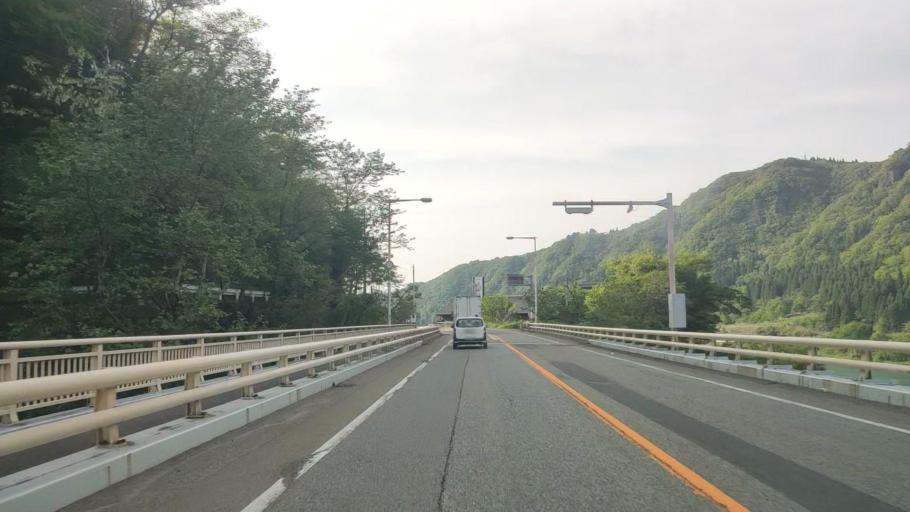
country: JP
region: Toyama
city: Yatsuomachi-higashikumisaka
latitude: 36.5454
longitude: 137.2277
